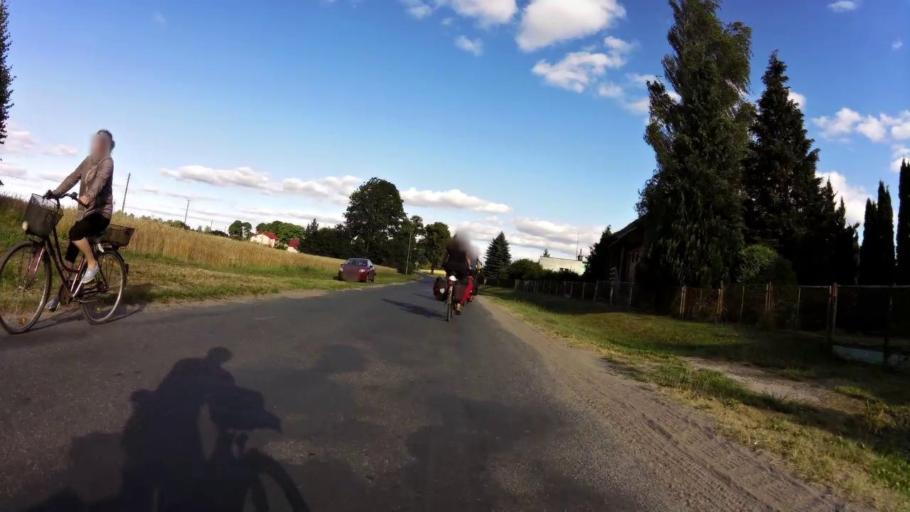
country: PL
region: West Pomeranian Voivodeship
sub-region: Powiat swidwinski
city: Swidwin
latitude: 53.6860
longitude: 15.7481
